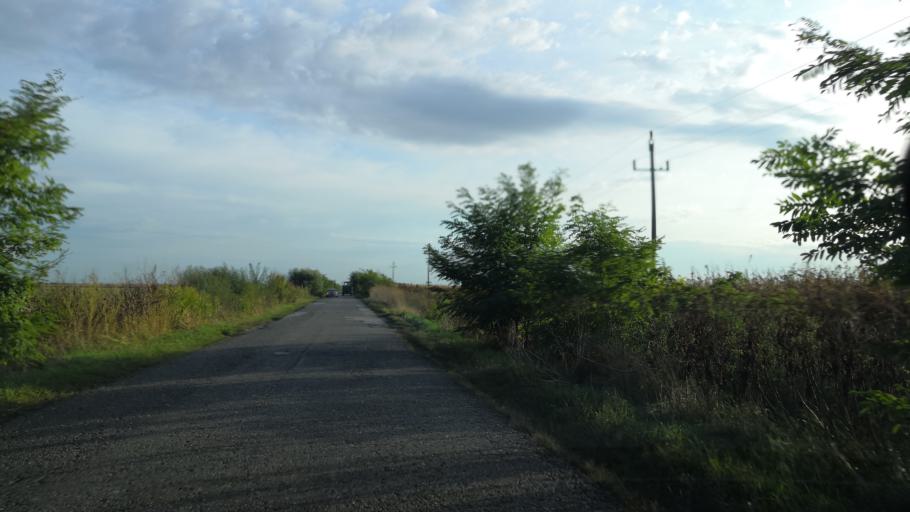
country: RS
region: Autonomna Pokrajina Vojvodina
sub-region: Sremski Okrug
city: Stara Pazova
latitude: 45.0130
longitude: 20.1680
